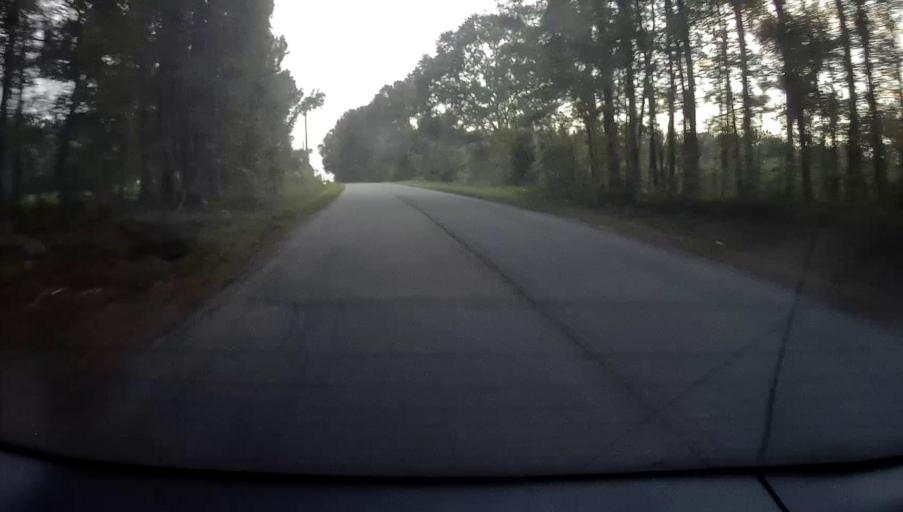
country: US
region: Georgia
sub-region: Butts County
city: Jackson
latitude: 33.2957
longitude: -84.0432
